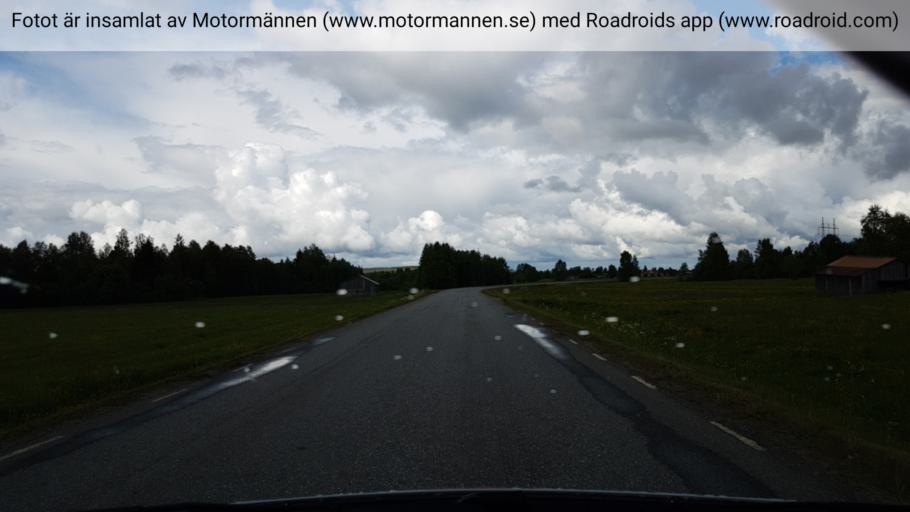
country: SE
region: Vaesterbotten
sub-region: Vannas Kommun
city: Vannasby
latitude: 63.9292
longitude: 19.8550
